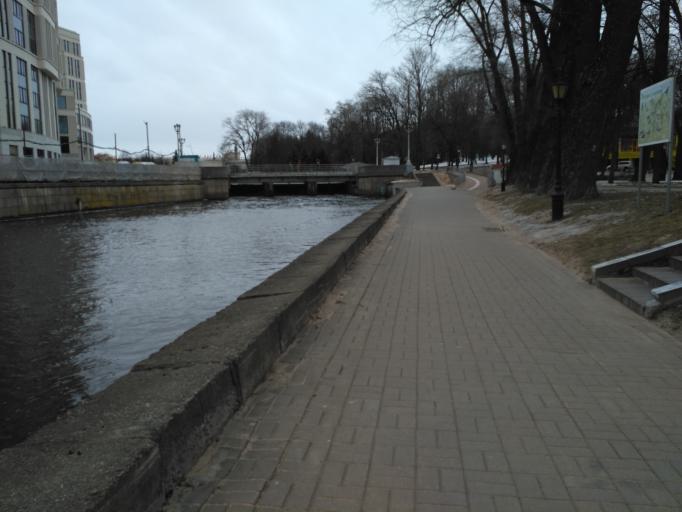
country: BY
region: Minsk
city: Minsk
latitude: 53.9037
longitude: 27.5697
